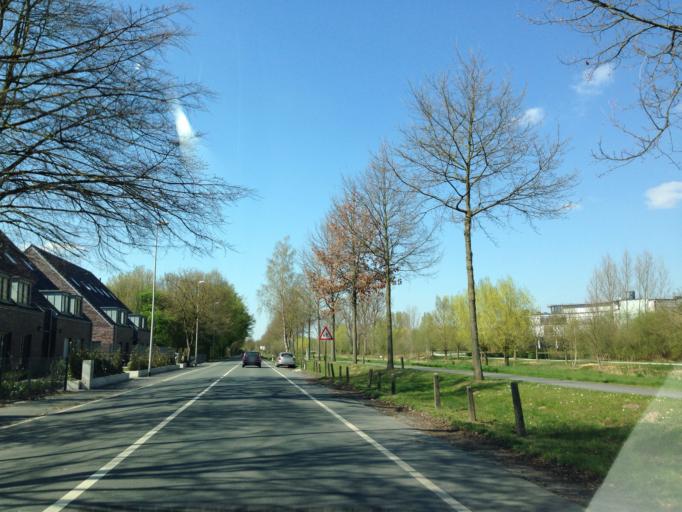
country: DE
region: North Rhine-Westphalia
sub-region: Regierungsbezirk Munster
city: Muenster
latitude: 51.9786
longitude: 7.6336
